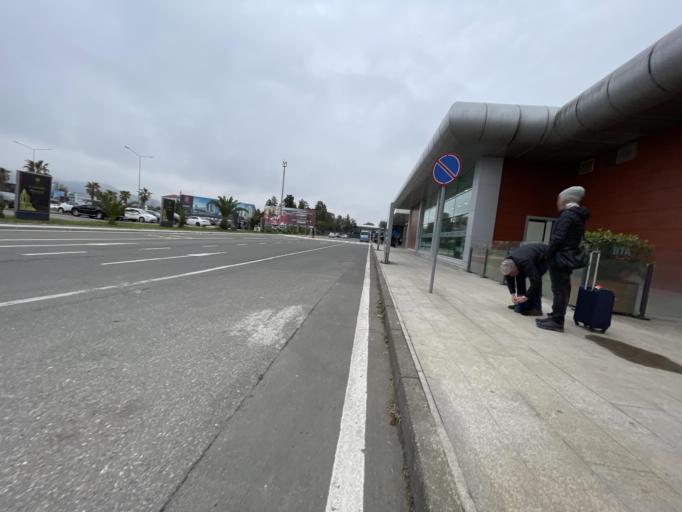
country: GE
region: Ajaria
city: Batumi
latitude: 41.6073
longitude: 41.6106
